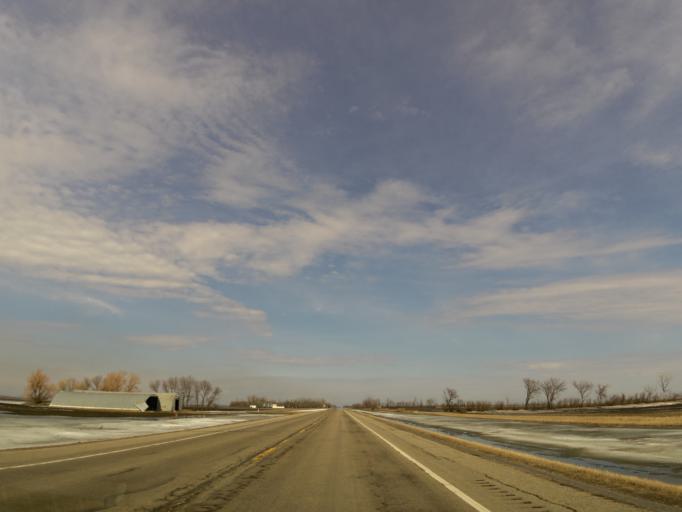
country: US
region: North Dakota
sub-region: Walsh County
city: Grafton
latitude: 48.3306
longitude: -97.4050
